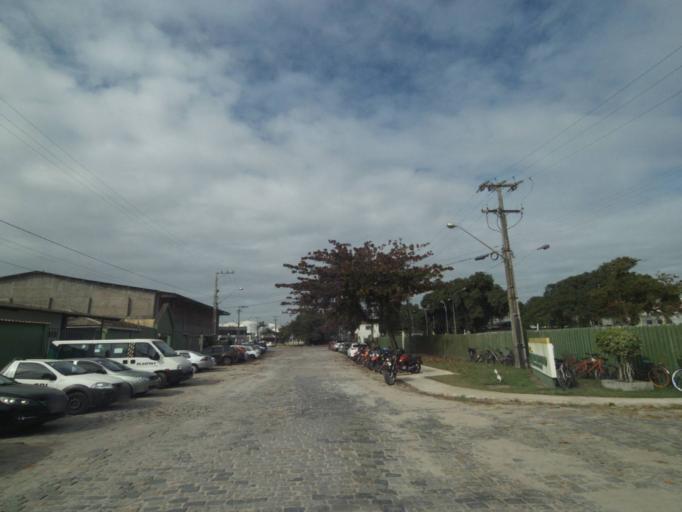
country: BR
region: Parana
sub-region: Paranagua
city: Paranagua
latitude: -25.5070
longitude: -48.5338
